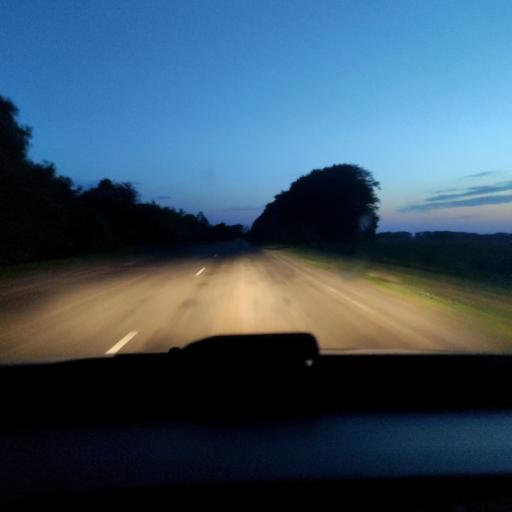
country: RU
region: Voronezj
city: Panino
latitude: 51.6365
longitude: 40.1011
